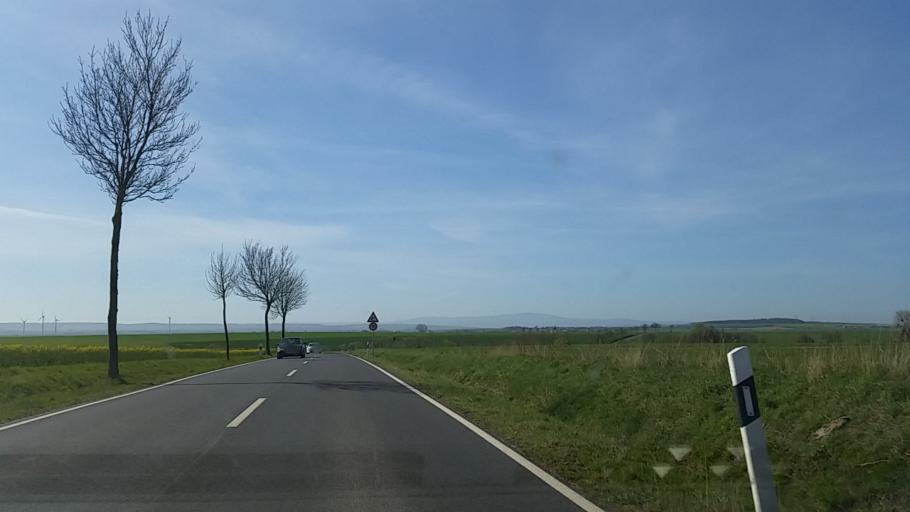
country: DE
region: Lower Saxony
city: Twieflingen
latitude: 52.1202
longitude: 10.9393
